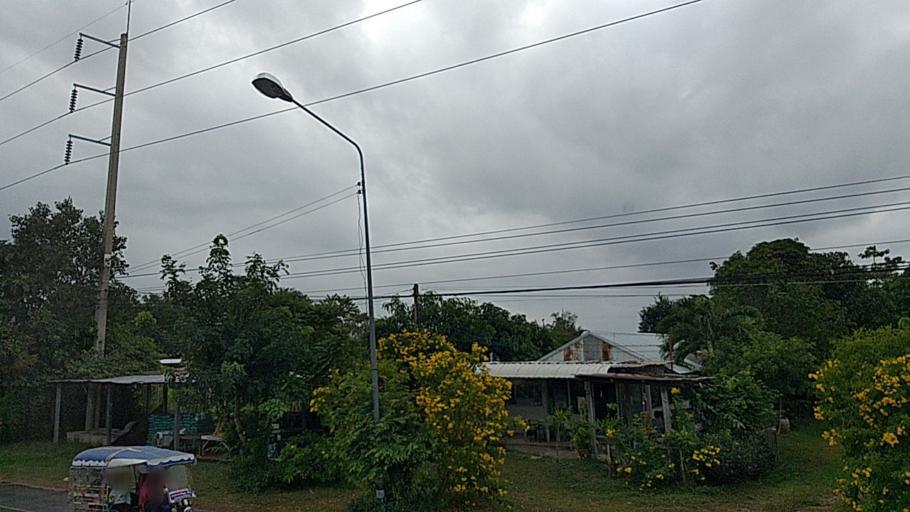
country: TH
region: Maha Sarakham
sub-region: Amphoe Borabue
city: Borabue
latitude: 16.0429
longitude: 103.1261
